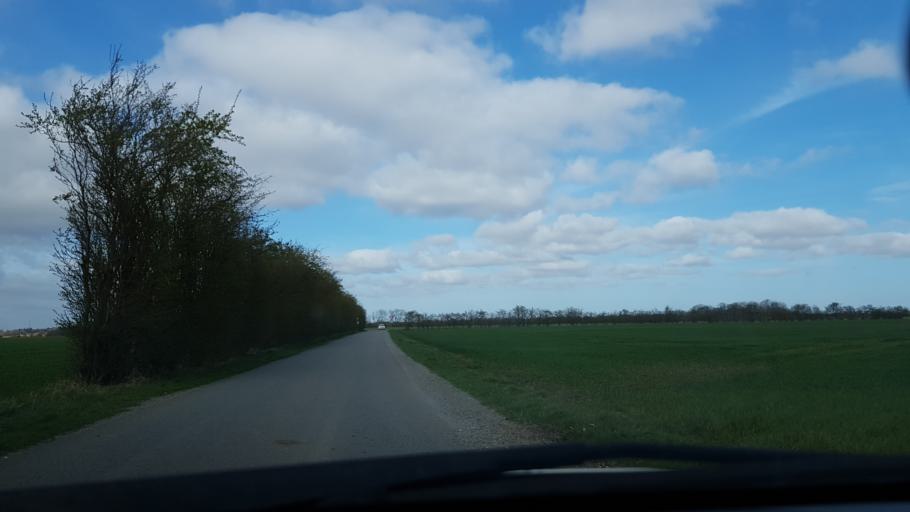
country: DK
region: South Denmark
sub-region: Vejen Kommune
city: Rodding
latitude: 55.3934
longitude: 9.0089
